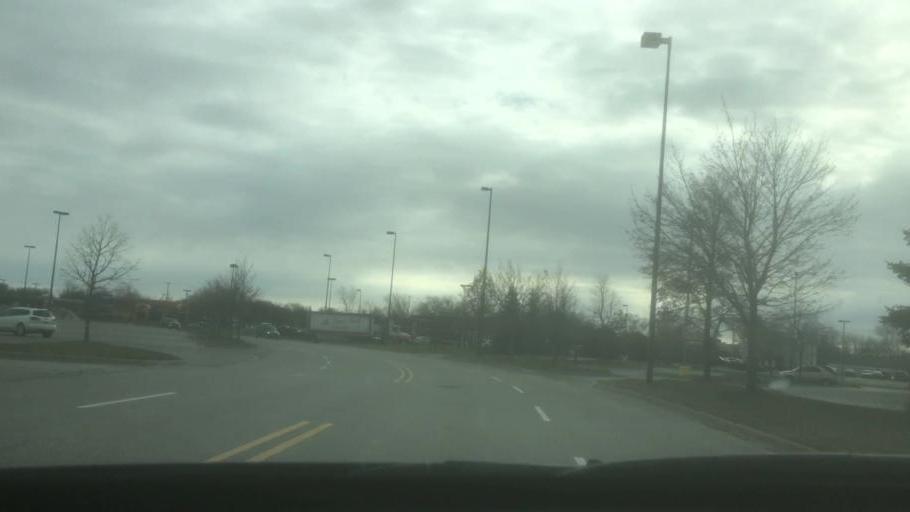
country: US
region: Michigan
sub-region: Bay County
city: Bay City
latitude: 43.6257
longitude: -83.8934
